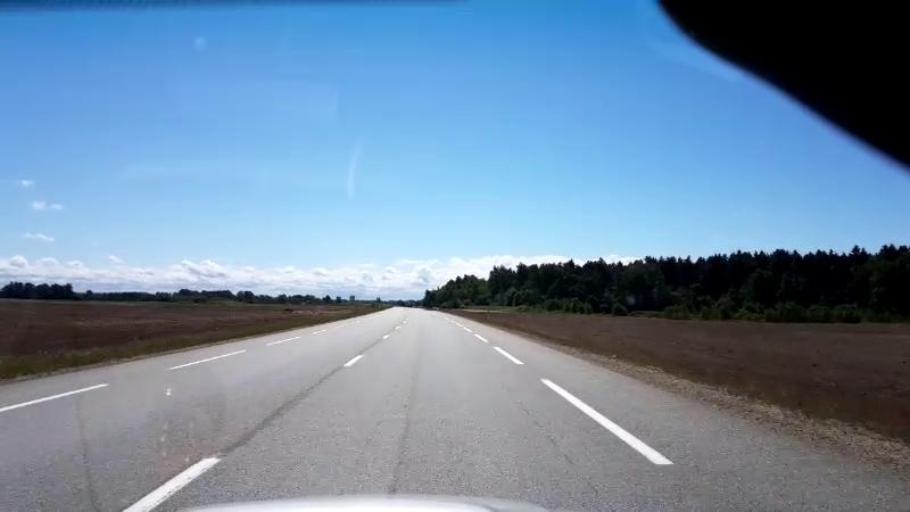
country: LV
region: Saulkrastu
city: Saulkrasti
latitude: 57.4139
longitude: 24.4304
